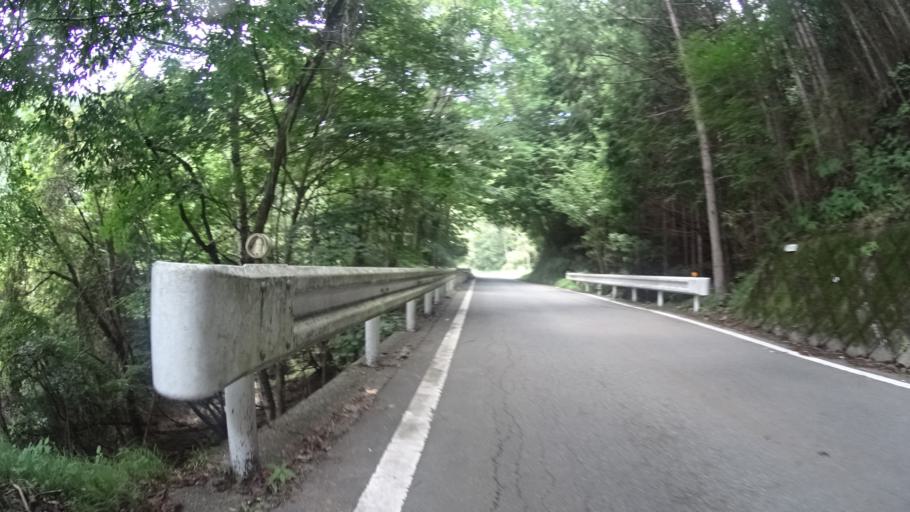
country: JP
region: Yamanashi
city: Enzan
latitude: 35.7985
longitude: 138.6823
